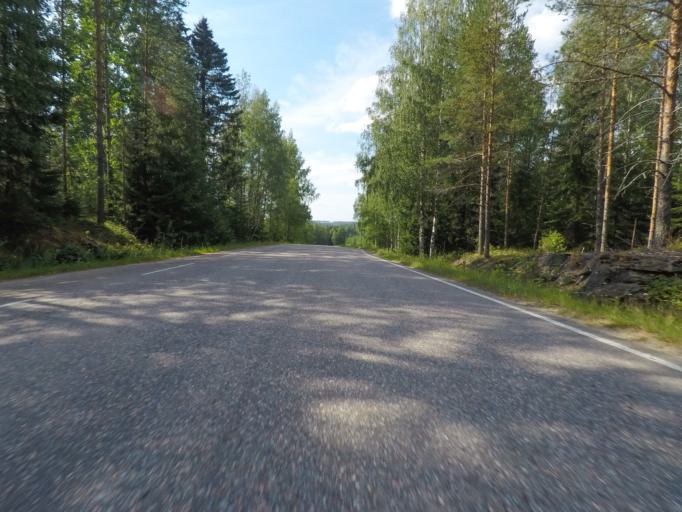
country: FI
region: Southern Savonia
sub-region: Mikkeli
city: Puumala
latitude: 61.6854
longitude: 28.2274
